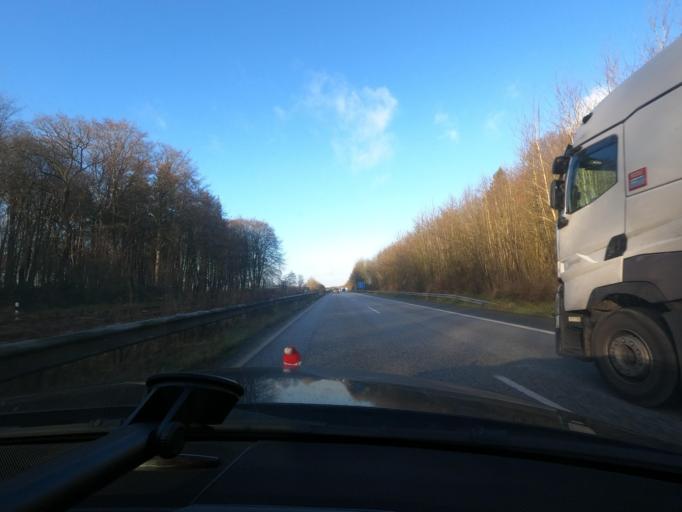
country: DE
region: Schleswig-Holstein
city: Schuby
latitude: 54.5139
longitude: 9.4966
